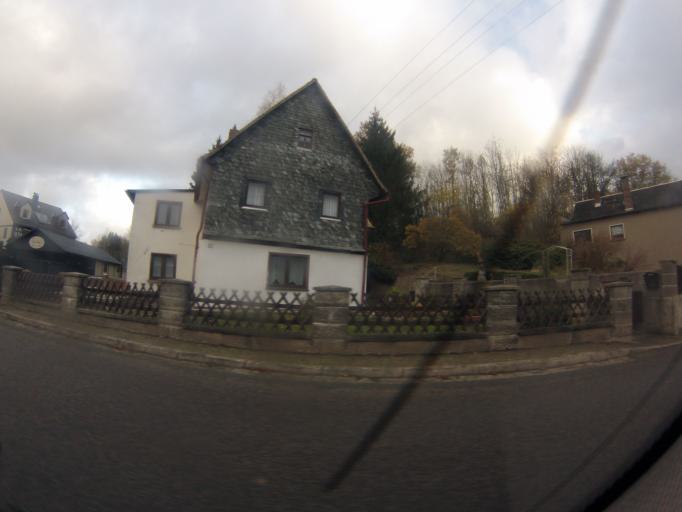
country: DE
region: Thuringia
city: Nobdenitz
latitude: 50.8555
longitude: 12.2871
